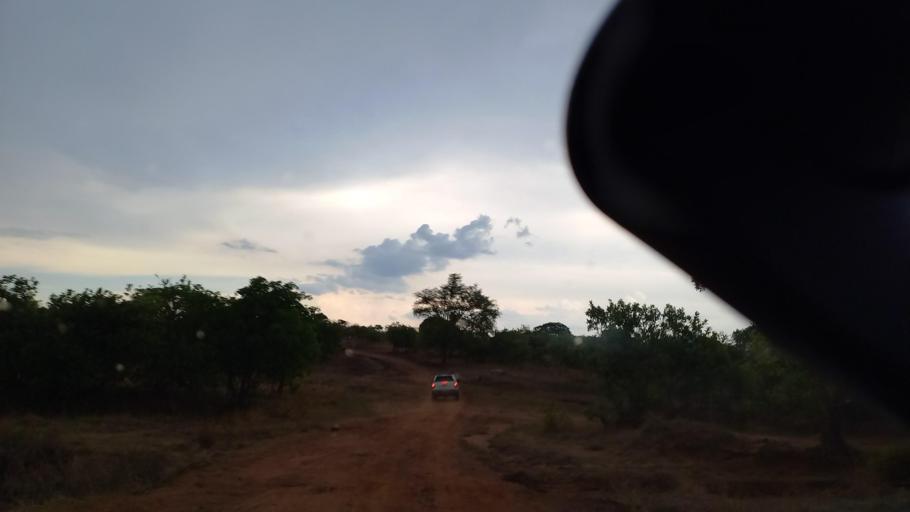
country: ZM
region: Lusaka
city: Kafue
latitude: -15.9863
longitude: 28.2654
